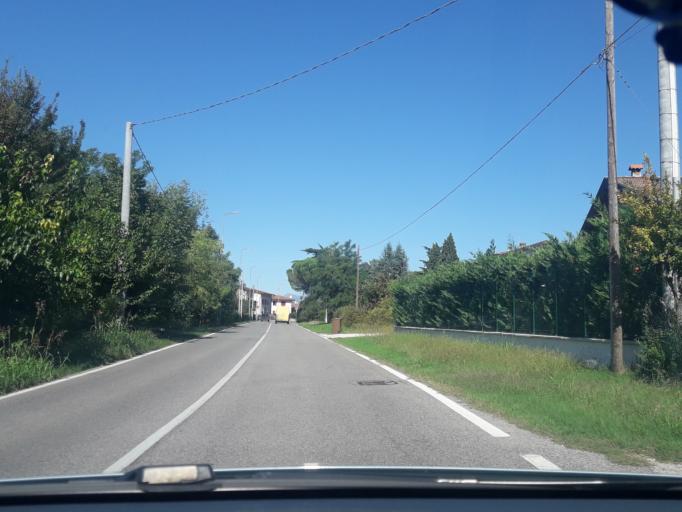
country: IT
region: Friuli Venezia Giulia
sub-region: Provincia di Udine
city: Basaldella
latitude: 46.0349
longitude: 13.2356
